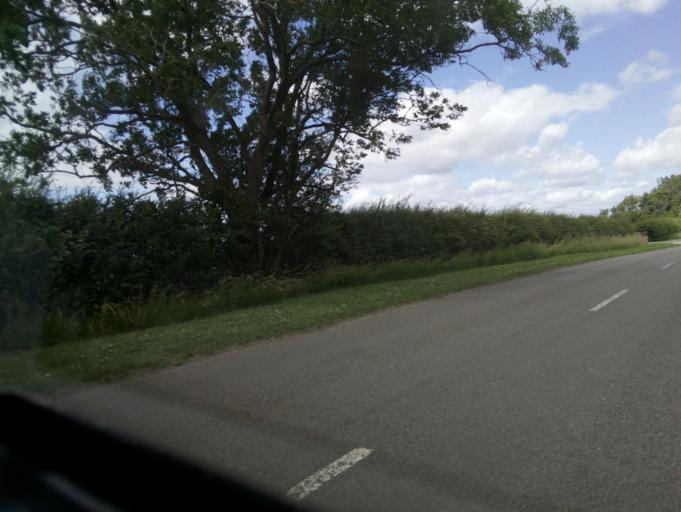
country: GB
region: England
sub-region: Nottinghamshire
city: Cotgrave
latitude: 52.8614
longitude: -1.0710
